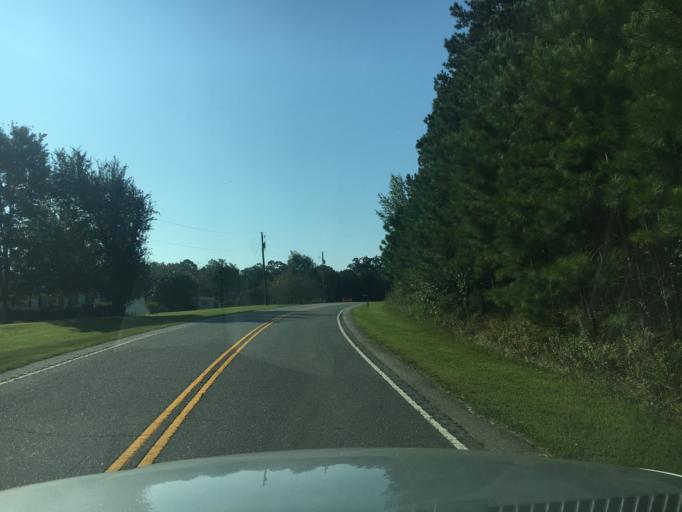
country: US
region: South Carolina
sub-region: Anderson County
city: Williamston
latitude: 34.6345
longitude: -82.3488
